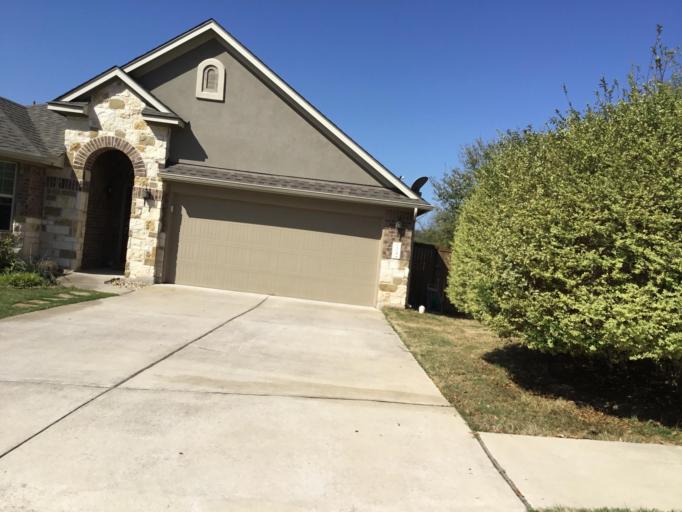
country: US
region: Texas
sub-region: Williamson County
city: Brushy Creek
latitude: 30.5723
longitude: -97.7715
